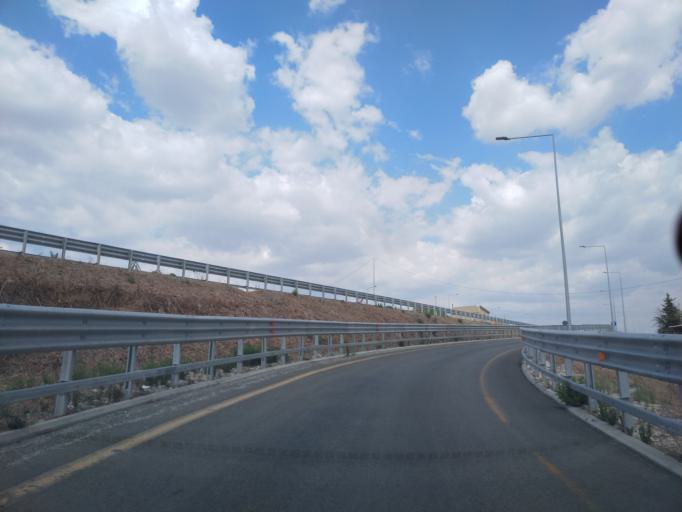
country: IT
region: Sicily
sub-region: Provincia di Caltanissetta
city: San Cataldo
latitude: 37.4502
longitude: 13.9705
